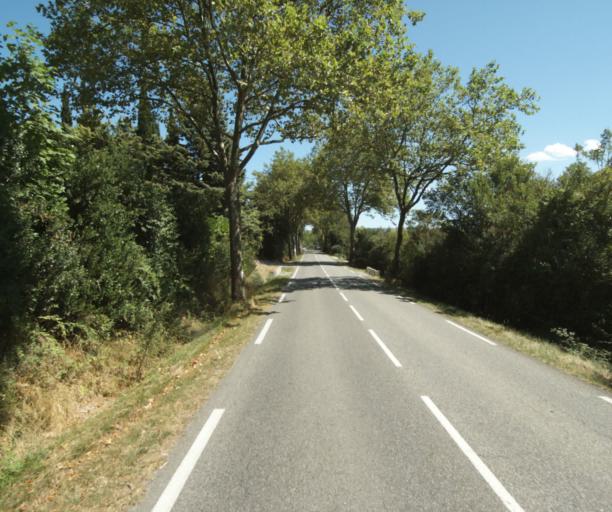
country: FR
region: Midi-Pyrenees
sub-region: Departement de la Haute-Garonne
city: Saint-Felix-Lauragais
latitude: 43.4797
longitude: 1.9200
